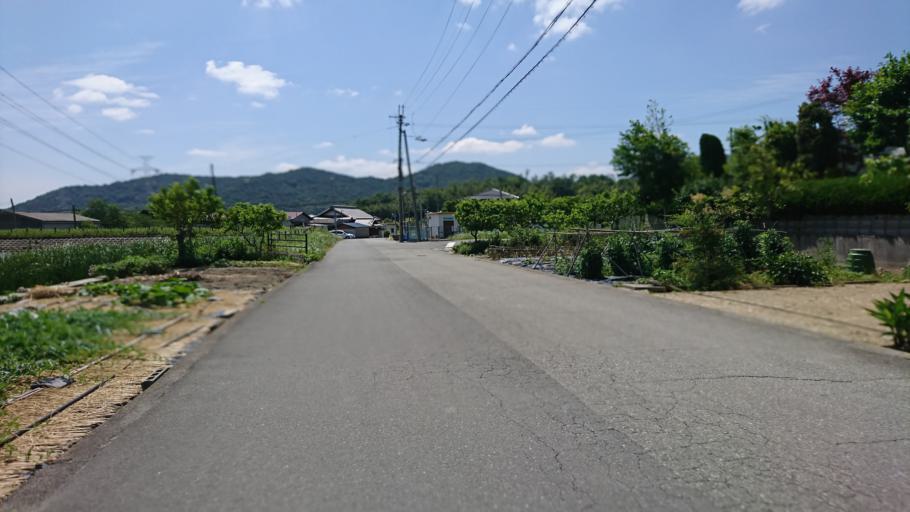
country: JP
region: Hyogo
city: Kakogawacho-honmachi
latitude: 34.8050
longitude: 134.7895
